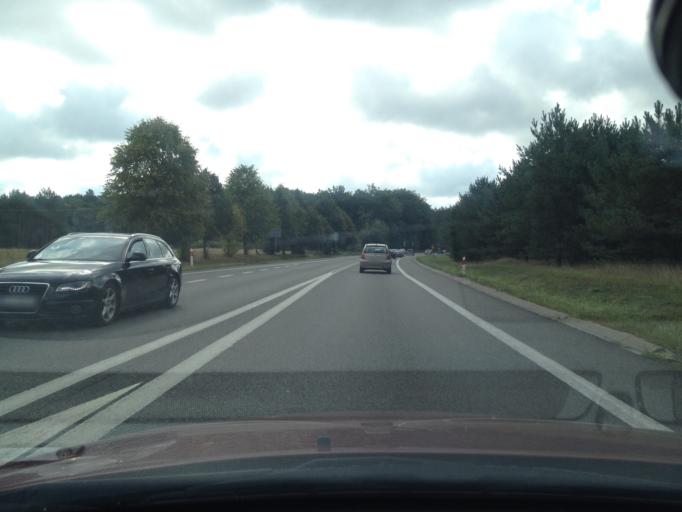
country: PL
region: West Pomeranian Voivodeship
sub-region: Powiat goleniowski
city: Przybiernow
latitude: 53.6777
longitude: 14.8120
